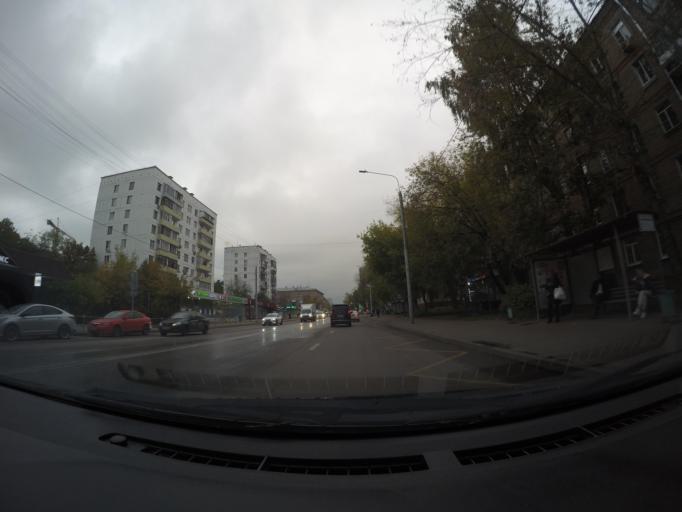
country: RU
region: Moscow
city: Perovo
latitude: 55.7582
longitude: 37.7956
